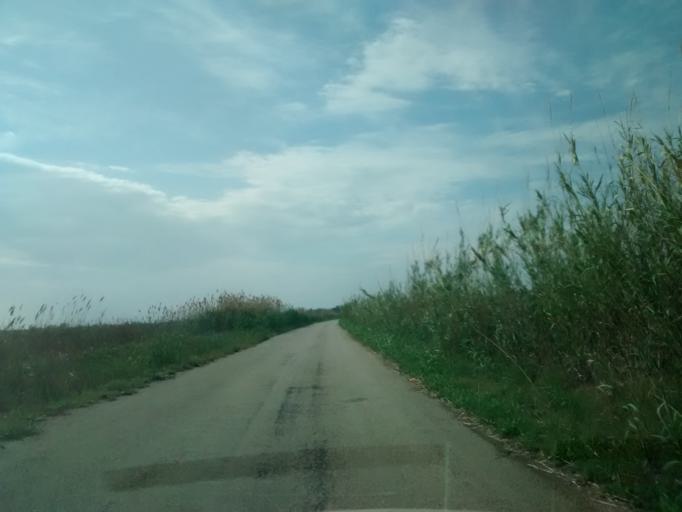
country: ES
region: Catalonia
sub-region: Provincia de Tarragona
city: Deltebre
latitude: 40.6902
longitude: 0.8449
